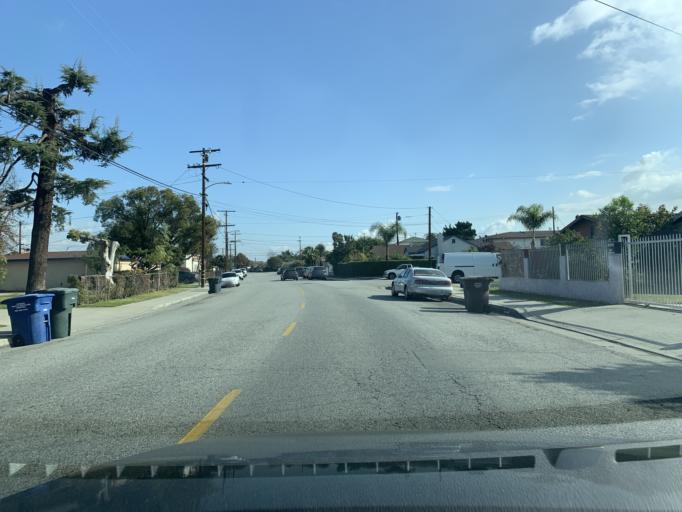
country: US
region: California
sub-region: Los Angeles County
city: South El Monte
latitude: 34.0654
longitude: -118.0535
